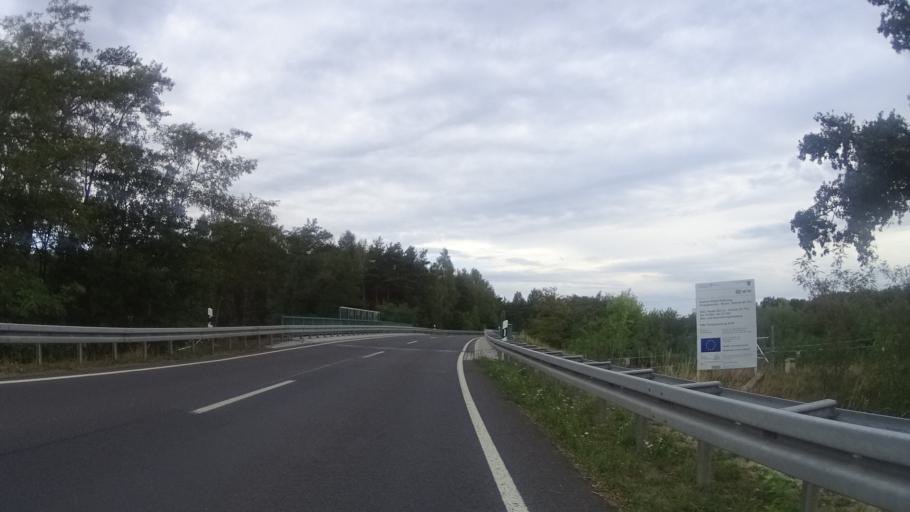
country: PL
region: Lower Silesian Voivodeship
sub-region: Powiat zgorzelecki
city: Piensk
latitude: 51.2854
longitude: 15.0238
